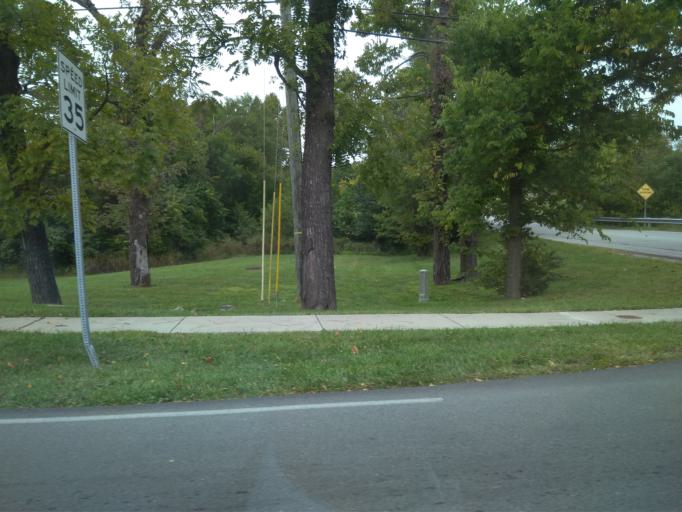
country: US
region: Kentucky
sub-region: Oldham County
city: Pewee Valley
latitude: 38.2833
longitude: -85.4860
